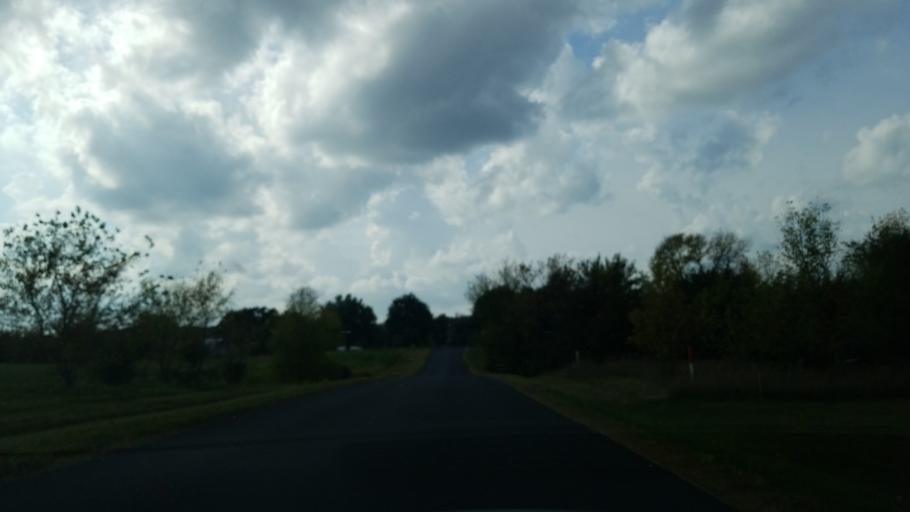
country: US
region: Minnesota
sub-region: Washington County
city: Lake Saint Croix Beach
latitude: 44.9056
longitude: -92.7336
